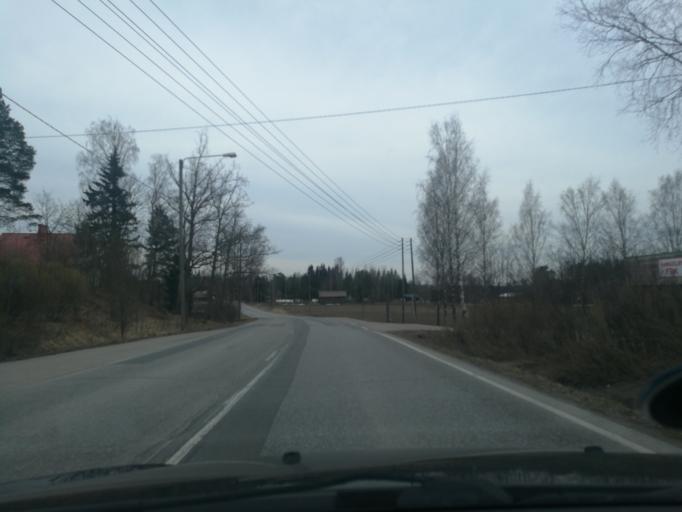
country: FI
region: Uusimaa
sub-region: Helsinki
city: Nickby
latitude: 60.2908
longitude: 25.3649
